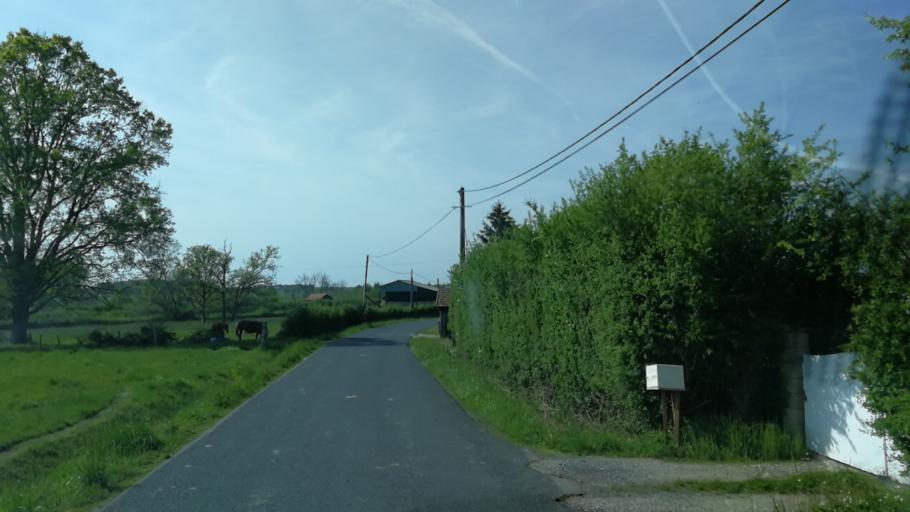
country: FR
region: Auvergne
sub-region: Departement de l'Allier
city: Neuilly-le-Real
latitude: 46.4664
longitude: 3.5370
